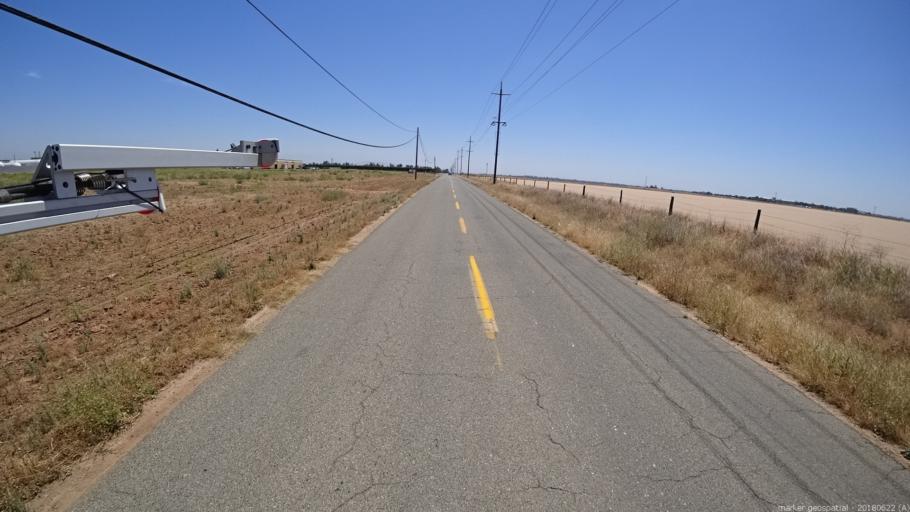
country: US
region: California
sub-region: Madera County
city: Bonadelle Ranchos-Madera Ranchos
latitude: 36.8949
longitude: -119.8139
